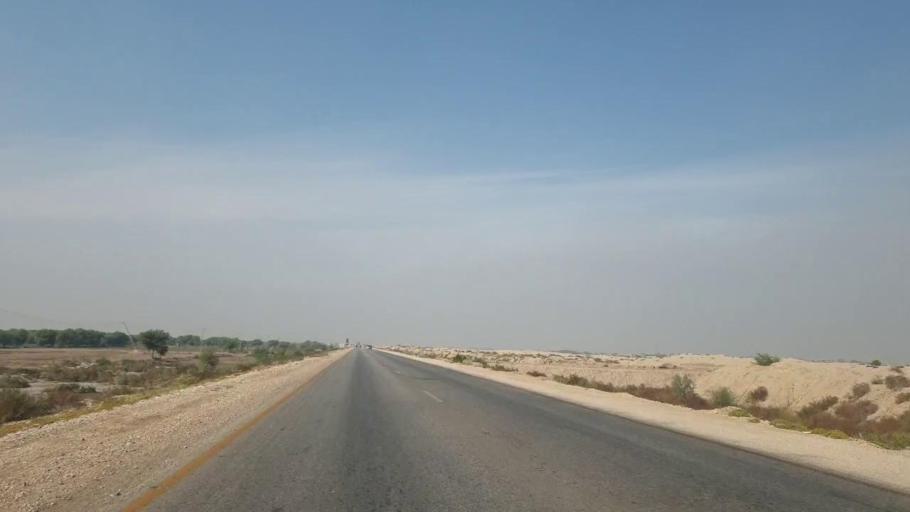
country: PK
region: Sindh
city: Sann
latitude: 25.9380
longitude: 68.2053
